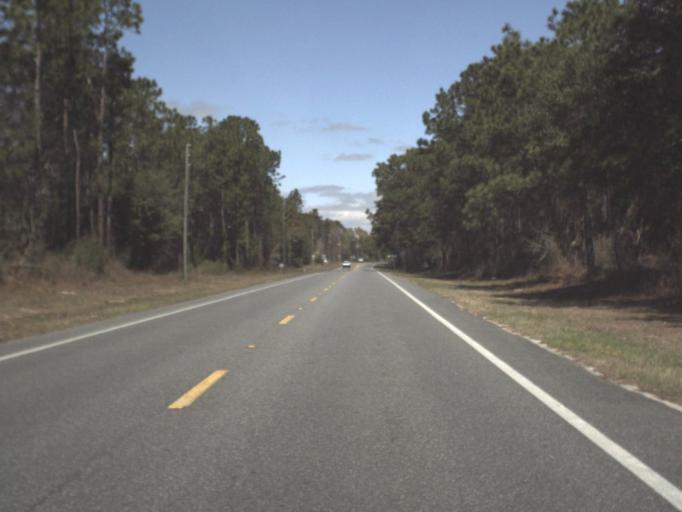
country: US
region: Florida
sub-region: Wakulla County
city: Crawfordville
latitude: 30.0736
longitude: -84.3892
